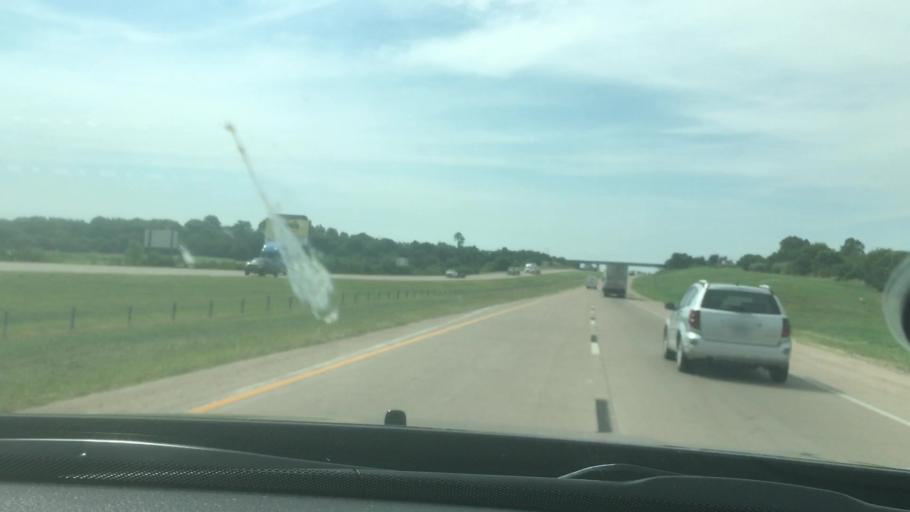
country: US
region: Oklahoma
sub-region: Garvin County
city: Pauls Valley
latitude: 34.7301
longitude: -97.2568
